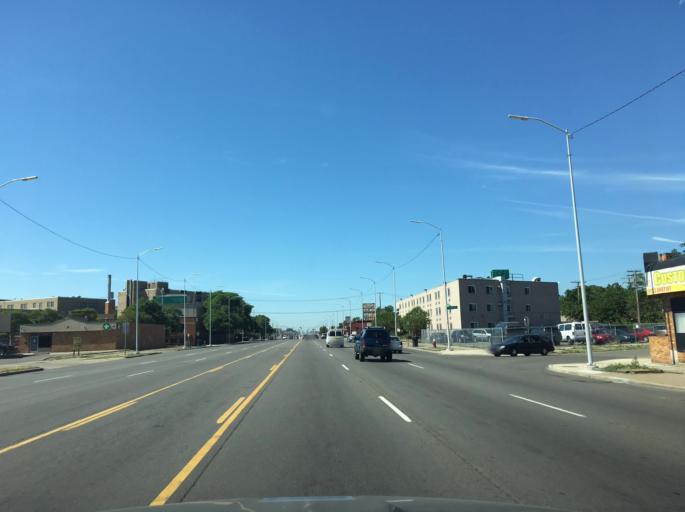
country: US
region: Michigan
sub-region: Macomb County
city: Eastpointe
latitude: 42.4455
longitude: -82.9708
